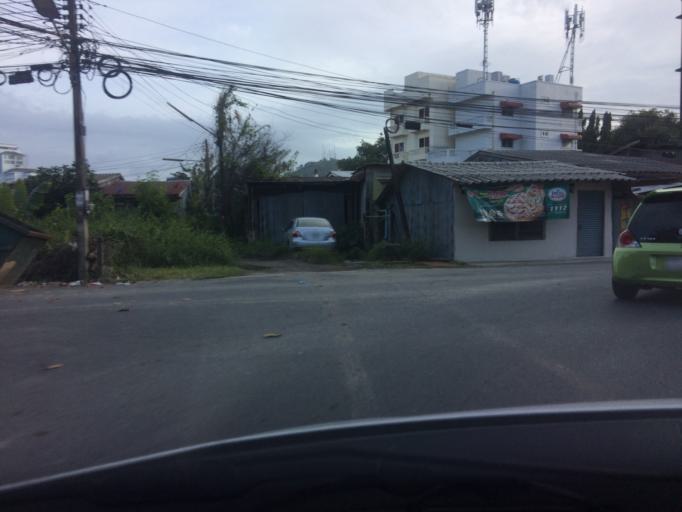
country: TH
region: Phuket
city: Ban Talat Yai
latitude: 7.8750
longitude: 98.3976
